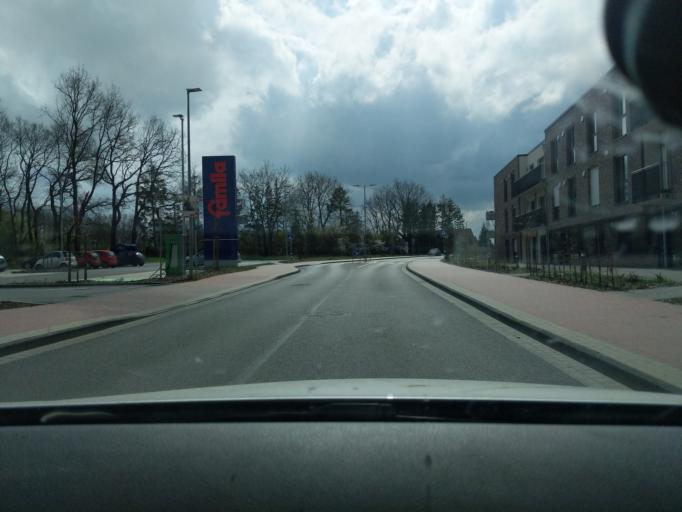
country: DE
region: Lower Saxony
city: Stade
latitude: 53.5702
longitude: 9.4708
